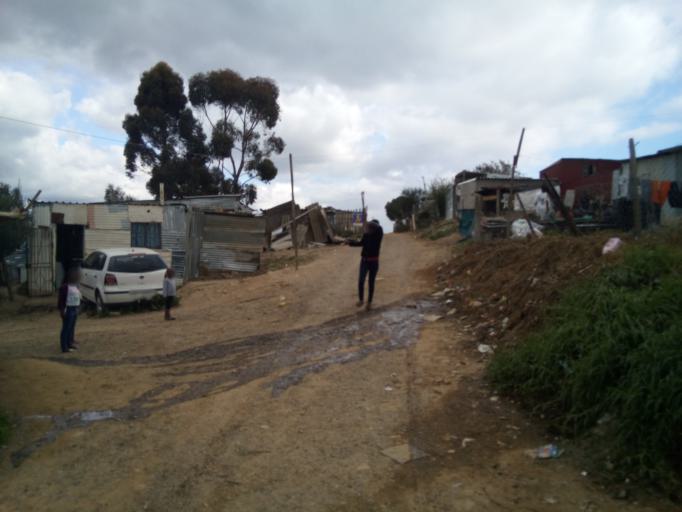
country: ZA
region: Western Cape
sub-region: Cape Winelands District Municipality
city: Stellenbosch
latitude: -33.9224
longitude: 18.8414
